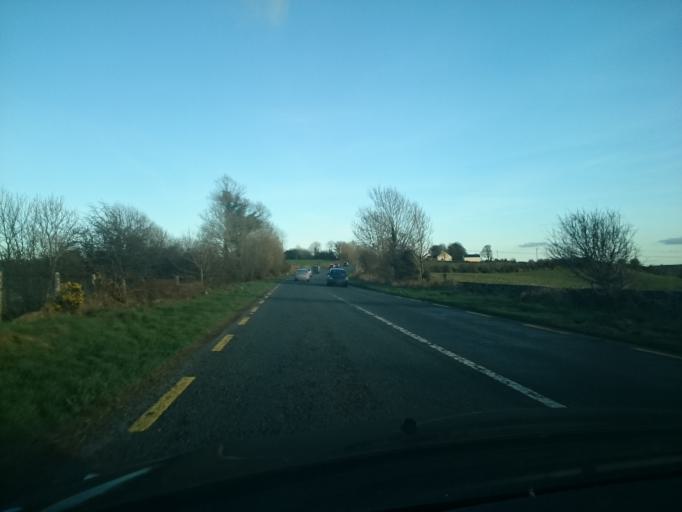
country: IE
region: Connaught
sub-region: Maigh Eo
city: Claremorris
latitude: 53.7629
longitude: -9.0452
